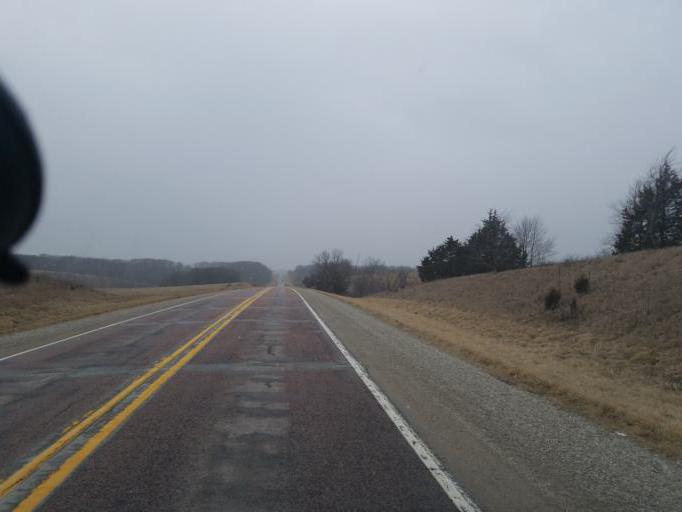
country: US
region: Iowa
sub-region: Appanoose County
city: Centerville
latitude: 40.6157
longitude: -92.9573
